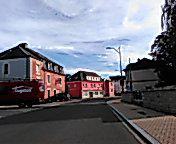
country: LU
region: Luxembourg
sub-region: Canton de Capellen
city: Steinfort
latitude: 49.6455
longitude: 5.9157
